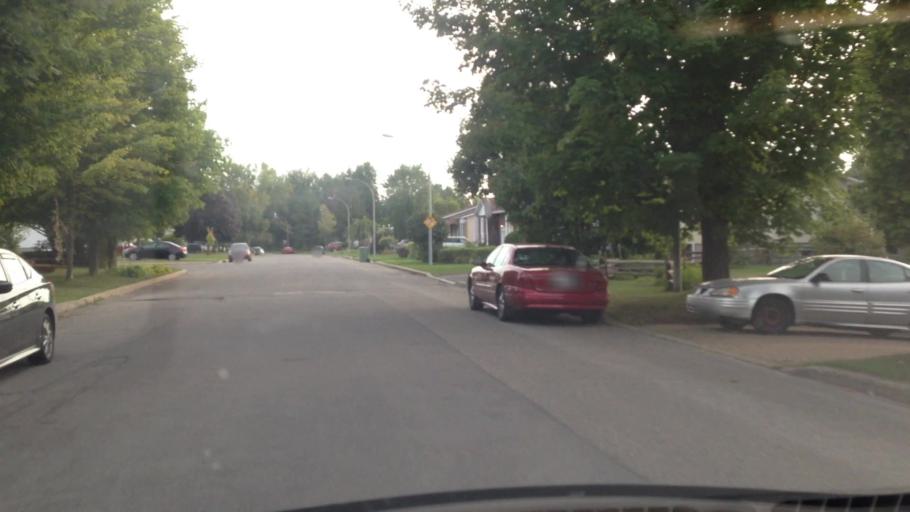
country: CA
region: Quebec
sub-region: Monteregie
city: Mercier
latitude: 45.3461
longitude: -73.7171
